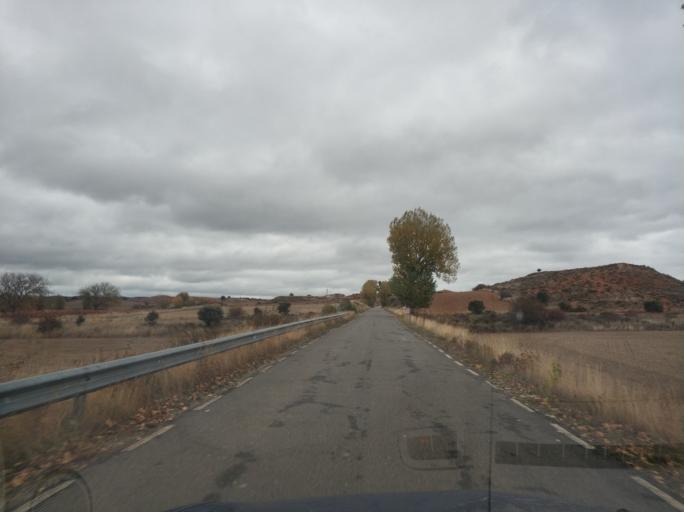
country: ES
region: Castille and Leon
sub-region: Provincia de Soria
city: San Esteban de Gormaz
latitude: 41.5925
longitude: -3.1742
